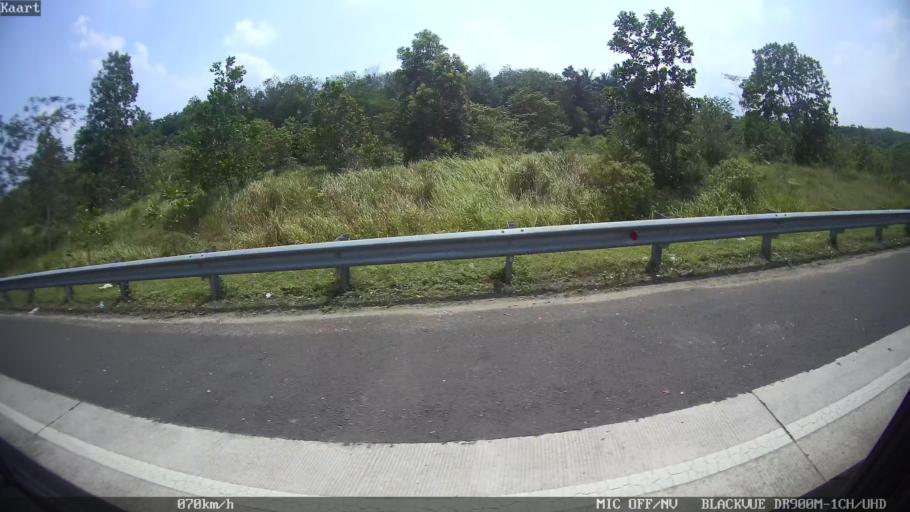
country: ID
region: Lampung
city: Kedaton
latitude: -5.3864
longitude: 105.3388
